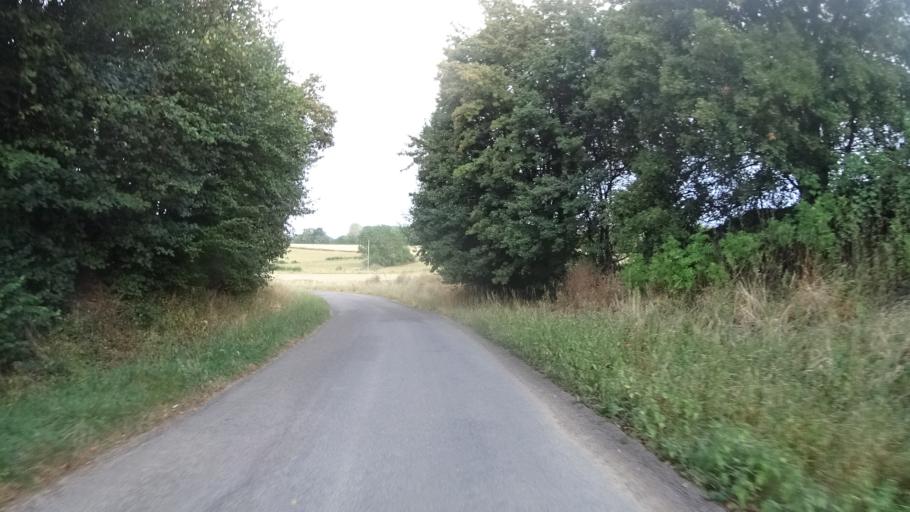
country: FR
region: Bourgogne
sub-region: Departement de Saone-et-Loire
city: Verdun-sur-le-Doubs
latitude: 46.9542
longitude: 5.0571
